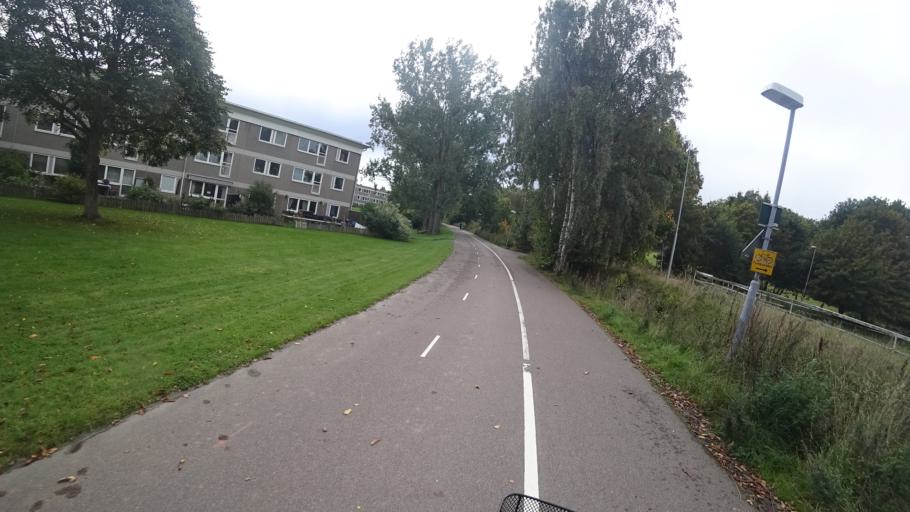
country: SE
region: Vaestra Goetaland
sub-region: Goteborg
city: Majorna
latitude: 57.6392
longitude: 11.9395
